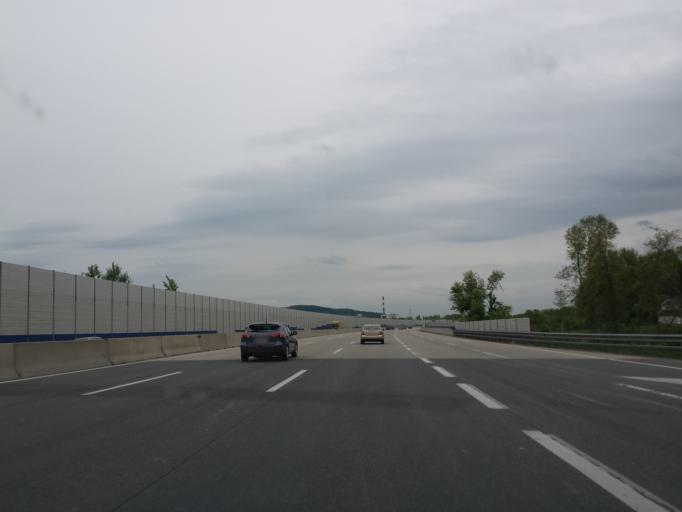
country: AT
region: Lower Austria
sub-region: Politischer Bezirk Korneuburg
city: Korneuburg
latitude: 48.3558
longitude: 16.3132
